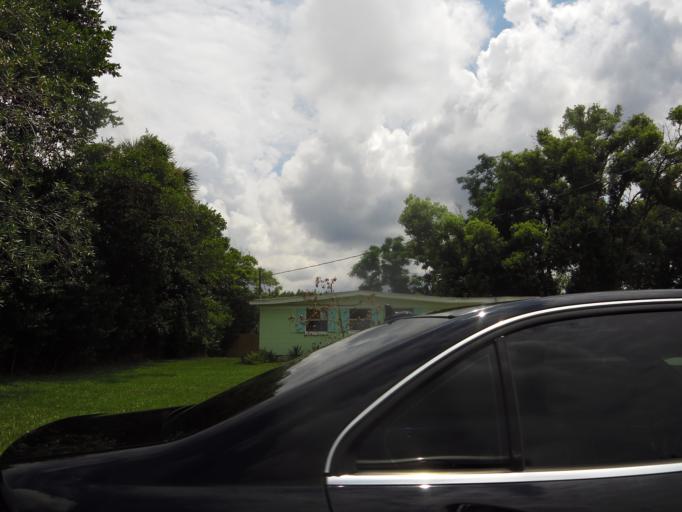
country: US
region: Florida
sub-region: Duval County
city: Atlantic Beach
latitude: 30.3297
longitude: -81.4156
